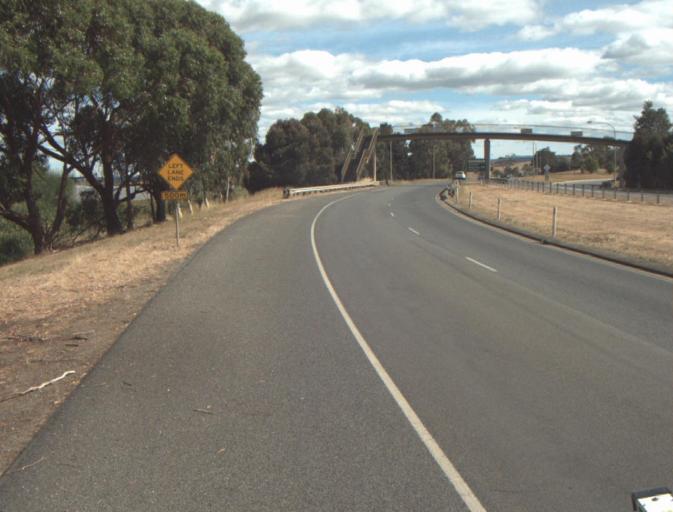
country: AU
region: Tasmania
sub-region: Launceston
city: Newnham
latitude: -41.4010
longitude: 147.1169
